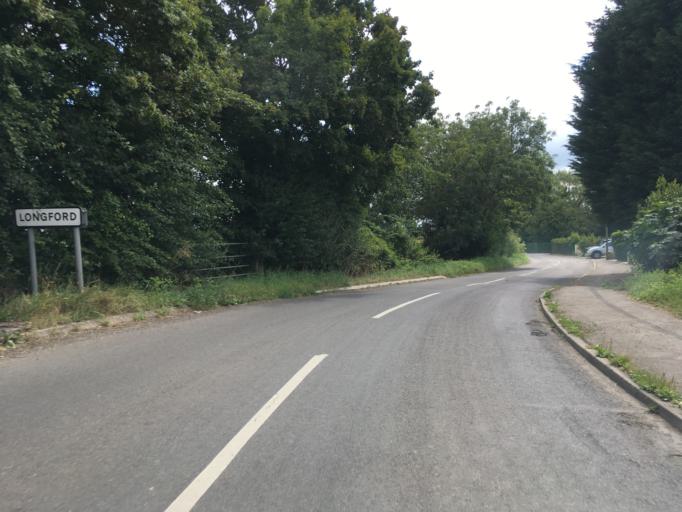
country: GB
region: England
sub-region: Gloucestershire
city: Gloucester
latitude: 51.8876
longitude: -2.2516
